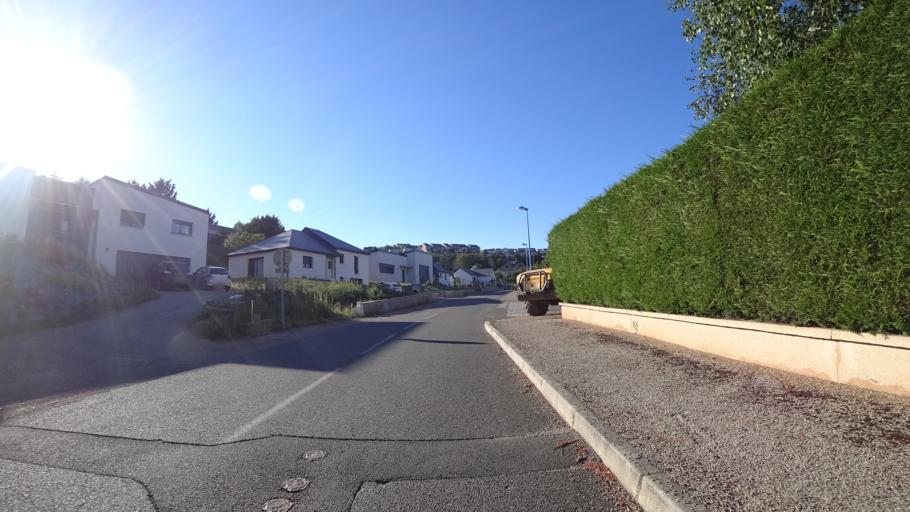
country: FR
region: Midi-Pyrenees
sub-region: Departement de l'Aveyron
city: Rodez
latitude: 44.3718
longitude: 2.5733
